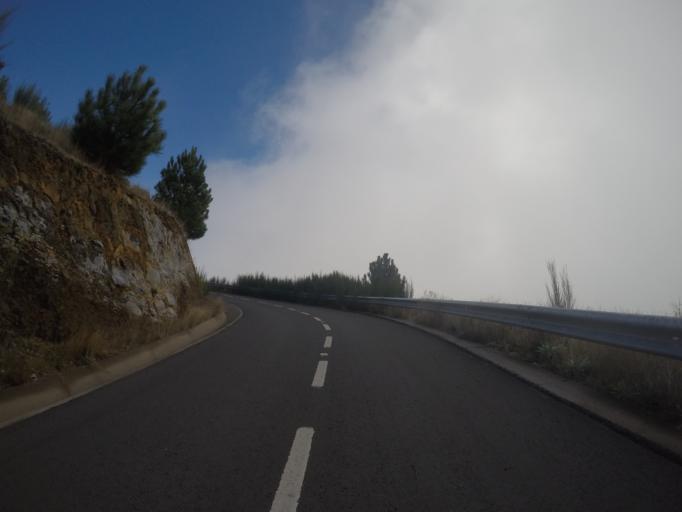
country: PT
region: Madeira
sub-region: Camara de Lobos
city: Curral das Freiras
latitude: 32.7117
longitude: -16.9549
